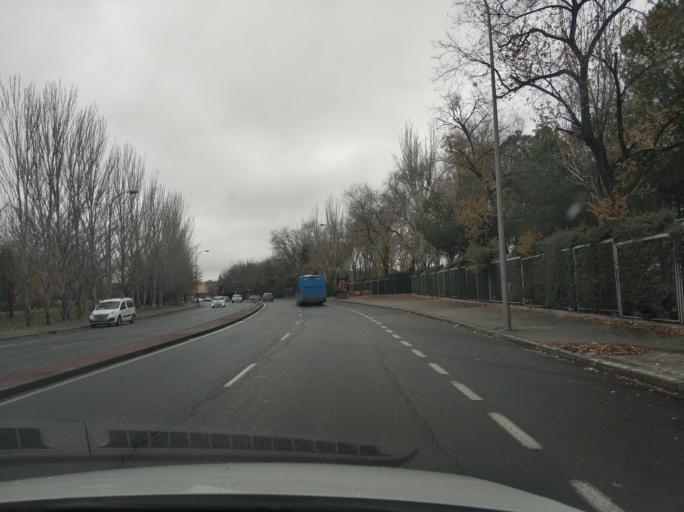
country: ES
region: Madrid
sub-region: Provincia de Madrid
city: Usera
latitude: 40.3737
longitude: -3.7135
